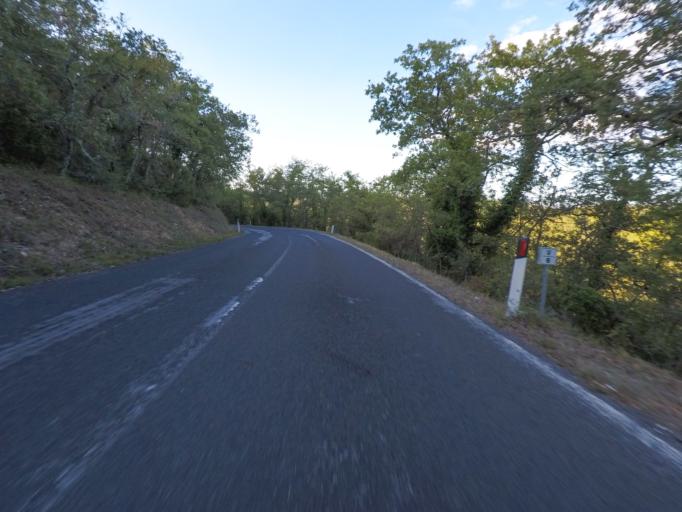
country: IT
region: Tuscany
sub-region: Provincia di Siena
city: Radda in Chianti
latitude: 43.4594
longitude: 11.3869
